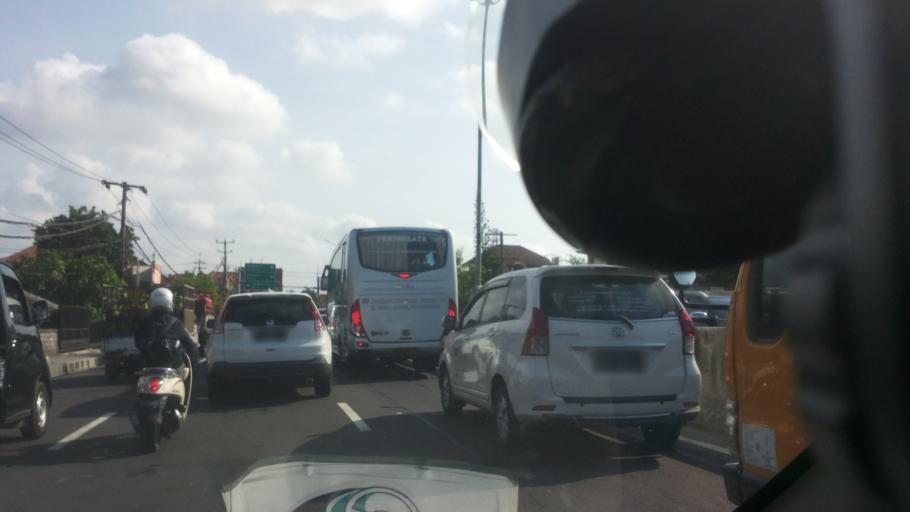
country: ID
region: Bali
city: Karyadharma
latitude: -8.7186
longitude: 115.2148
